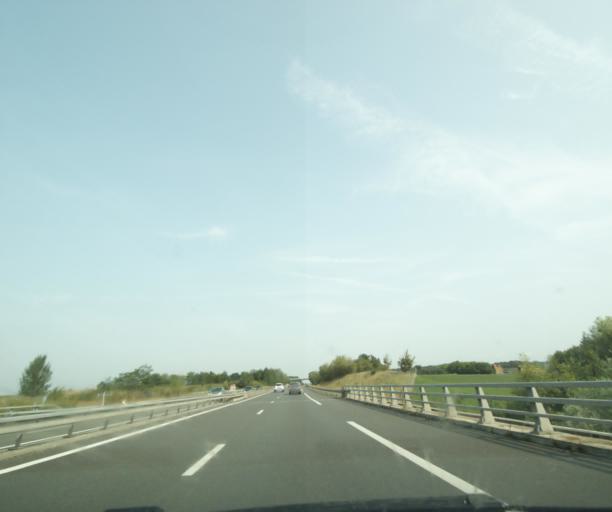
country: FR
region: Pays de la Loire
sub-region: Departement de la Sarthe
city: Beaumont-sur-Sarthe
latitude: 48.2815
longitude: 0.1563
